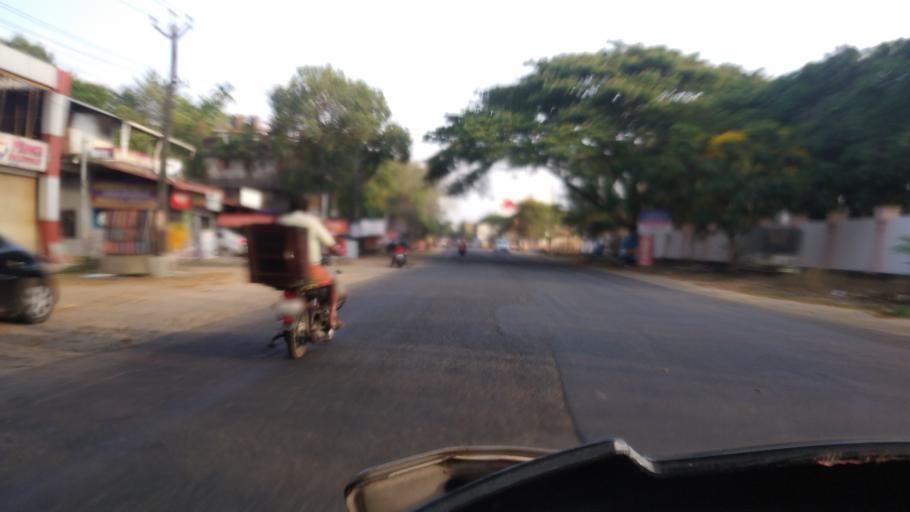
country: IN
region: Kerala
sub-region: Thrissur District
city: Thanniyam
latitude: 10.4240
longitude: 76.1031
